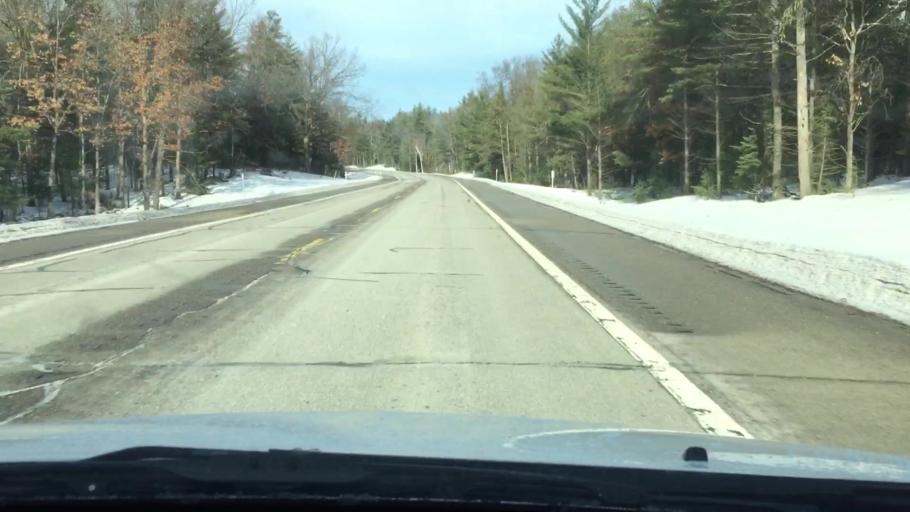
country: US
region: Michigan
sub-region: Wexford County
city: Manton
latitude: 44.5432
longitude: -85.3729
